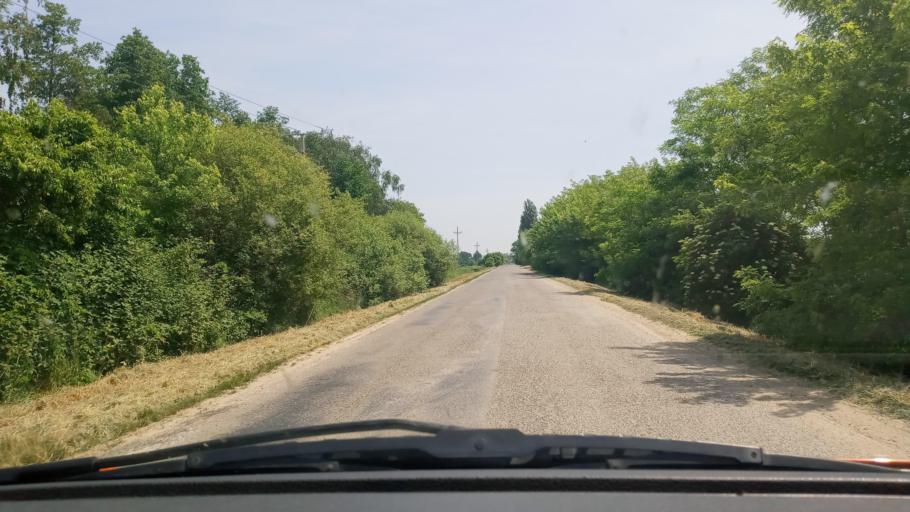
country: HU
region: Baranya
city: Szigetvar
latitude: 45.9657
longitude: 17.6983
